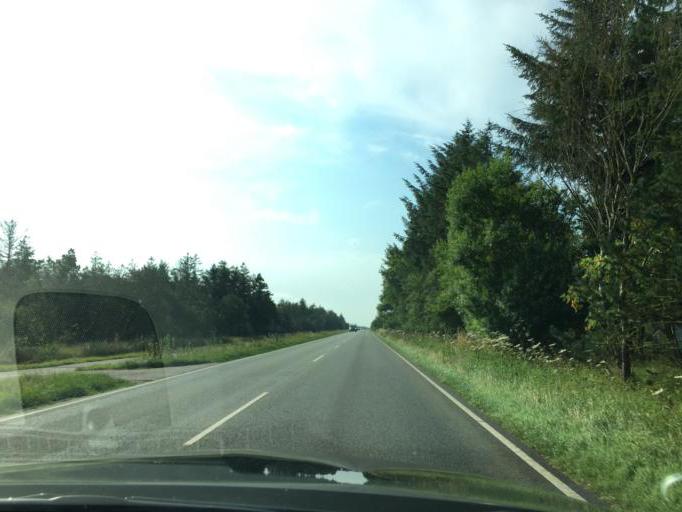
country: DK
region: South Denmark
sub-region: Varde Kommune
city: Oksbol
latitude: 55.7637
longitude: 8.3155
